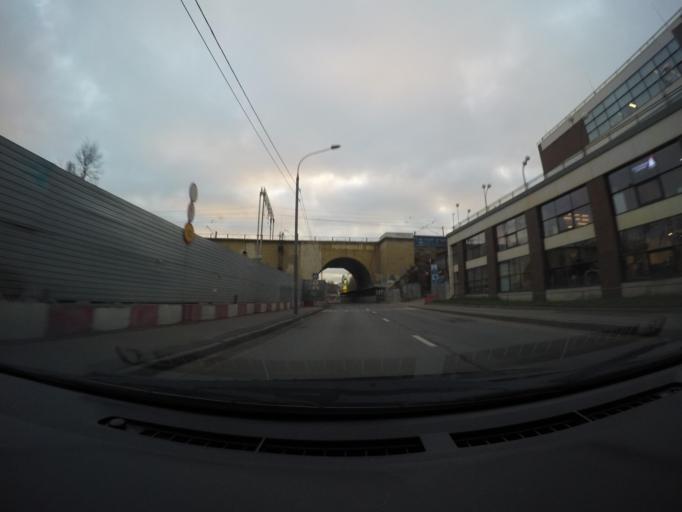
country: RU
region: Moscow
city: Taganskiy
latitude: 55.7514
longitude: 37.6710
